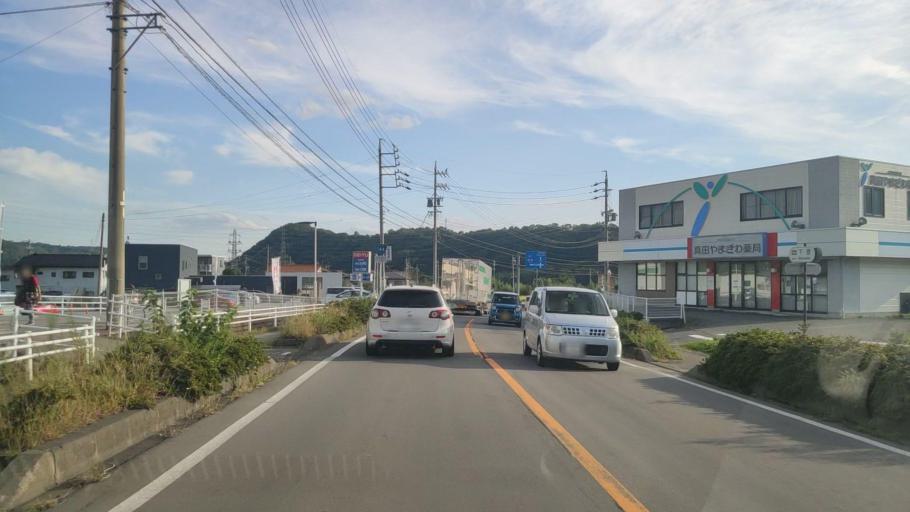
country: JP
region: Nagano
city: Ueda
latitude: 36.4213
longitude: 138.2993
